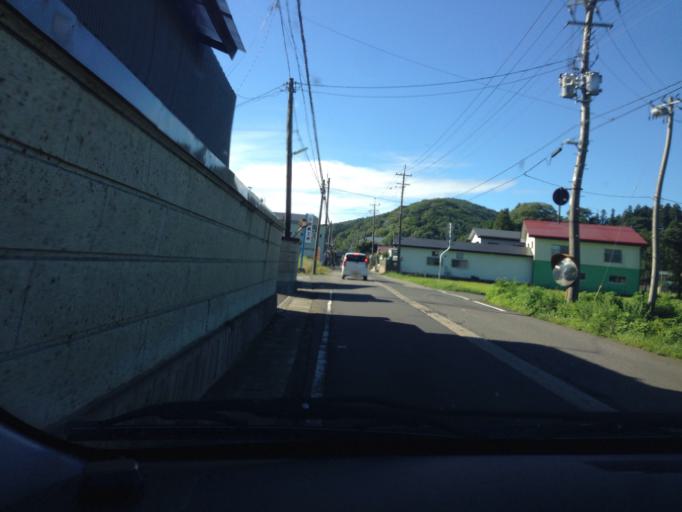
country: JP
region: Fukushima
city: Inawashiro
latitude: 37.3986
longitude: 140.1305
